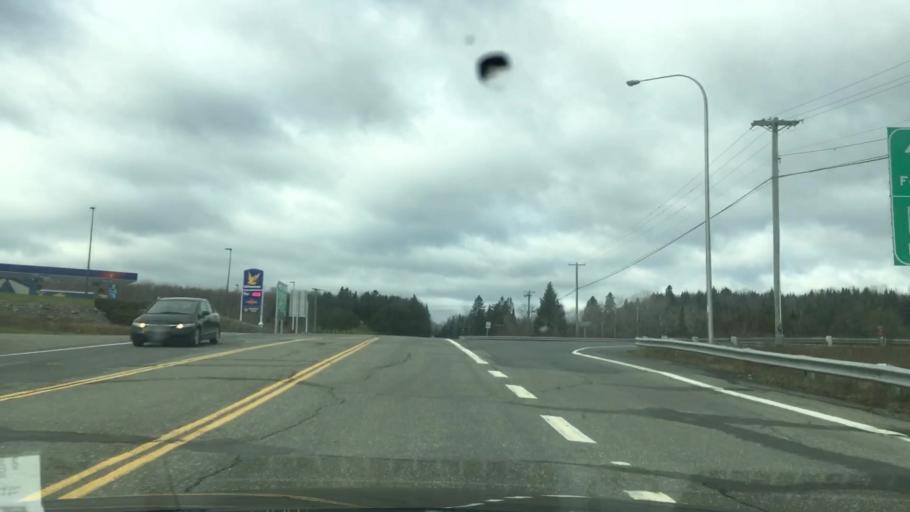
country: US
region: Maine
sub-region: Aroostook County
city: Fort Fairfield
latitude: 46.7494
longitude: -67.7178
